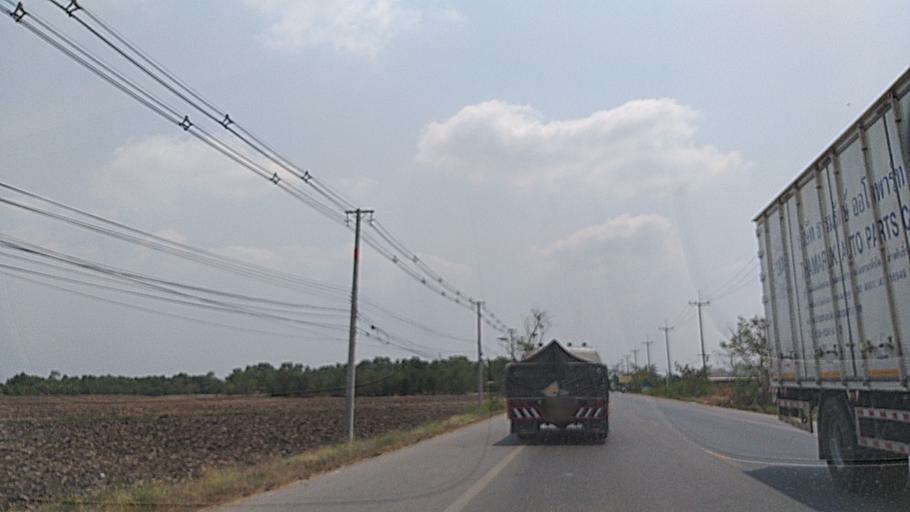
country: TH
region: Chachoengsao
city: Chachoengsao
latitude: 13.7365
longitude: 101.0858
